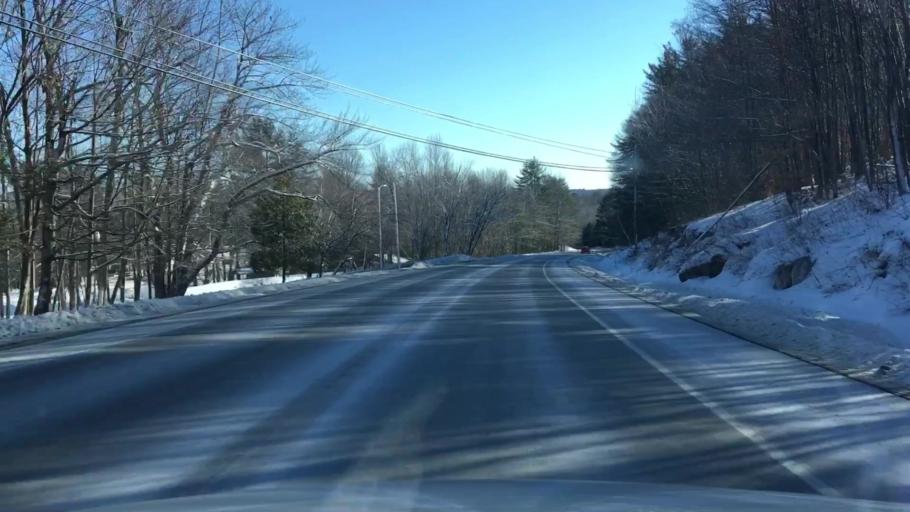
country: US
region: Maine
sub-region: Kennebec County
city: Readfield
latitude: 44.3979
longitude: -69.9915
